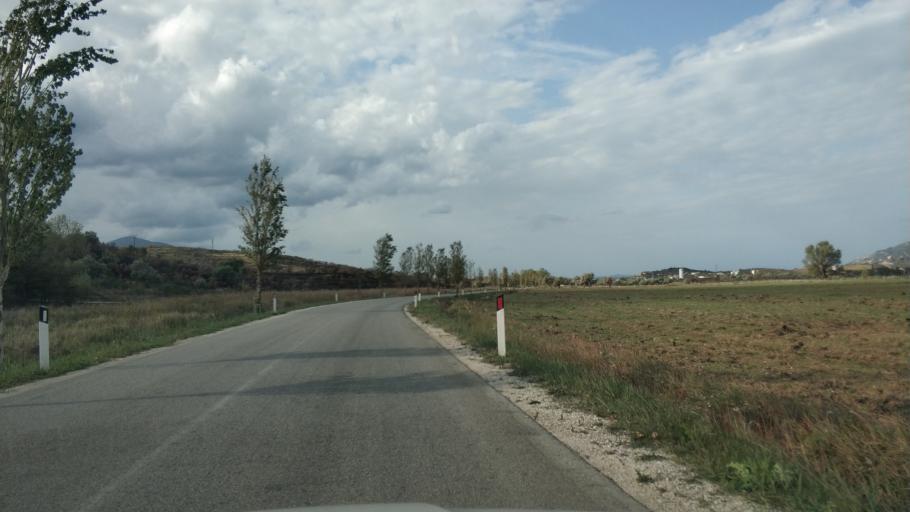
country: AL
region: Vlore
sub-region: Rrethi i Vlores
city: Orikum
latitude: 40.3155
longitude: 19.4852
